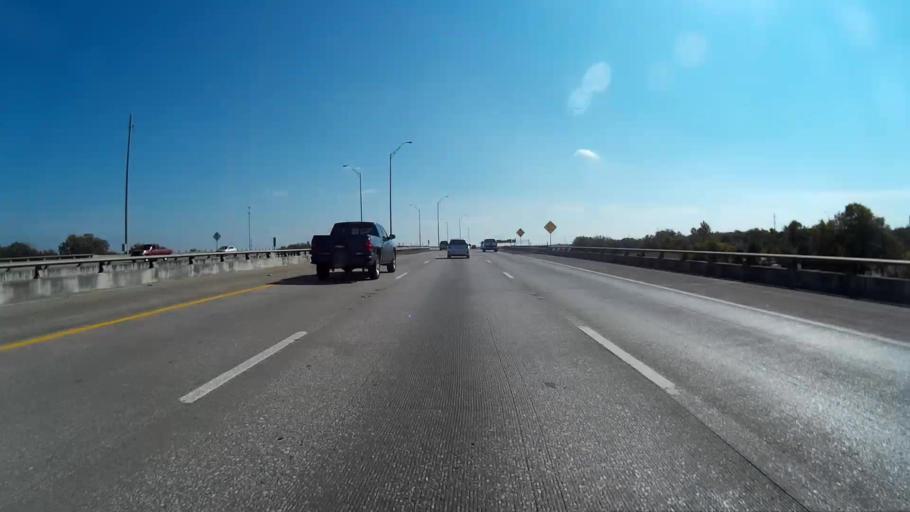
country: US
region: Texas
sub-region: Dallas County
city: Hutchins
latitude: 32.7147
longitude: -96.7574
